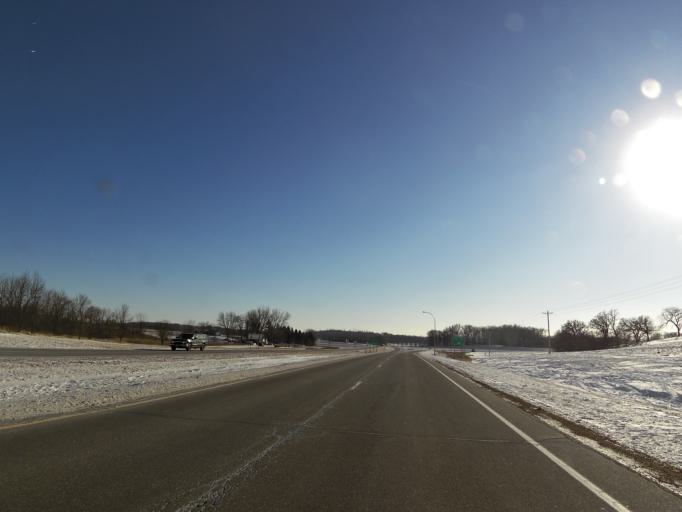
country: US
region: Minnesota
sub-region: Le Sueur County
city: New Prague
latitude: 44.5477
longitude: -93.5020
